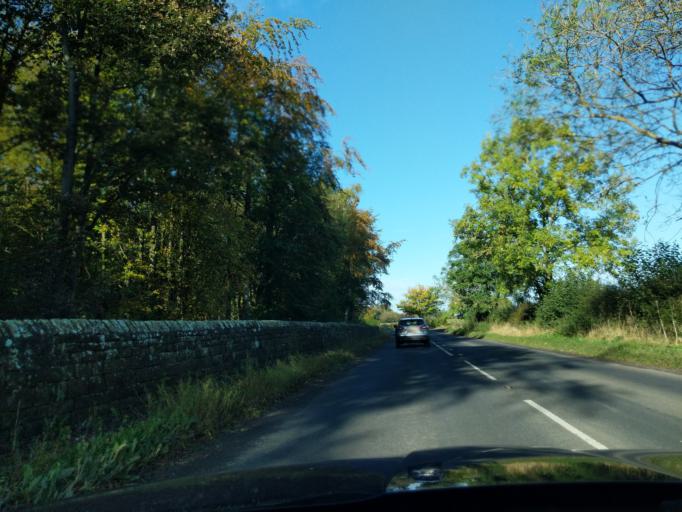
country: GB
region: England
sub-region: Northumberland
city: Stannington
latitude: 55.0872
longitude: -1.6531
